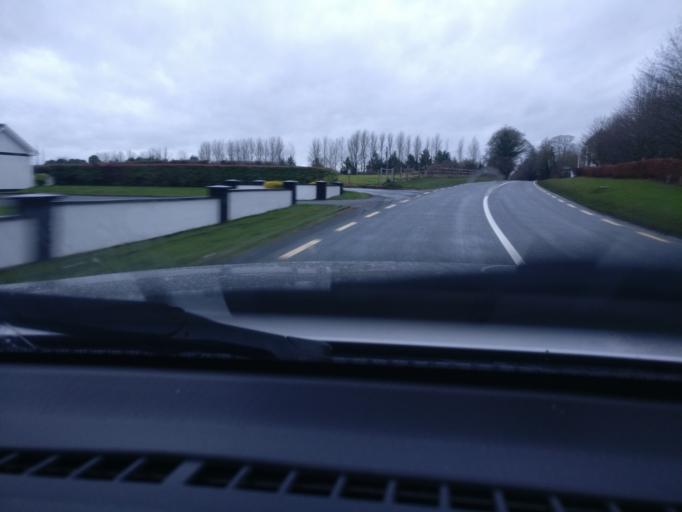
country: IE
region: Leinster
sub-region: An Mhi
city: Trim
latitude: 53.5217
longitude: -6.8234
